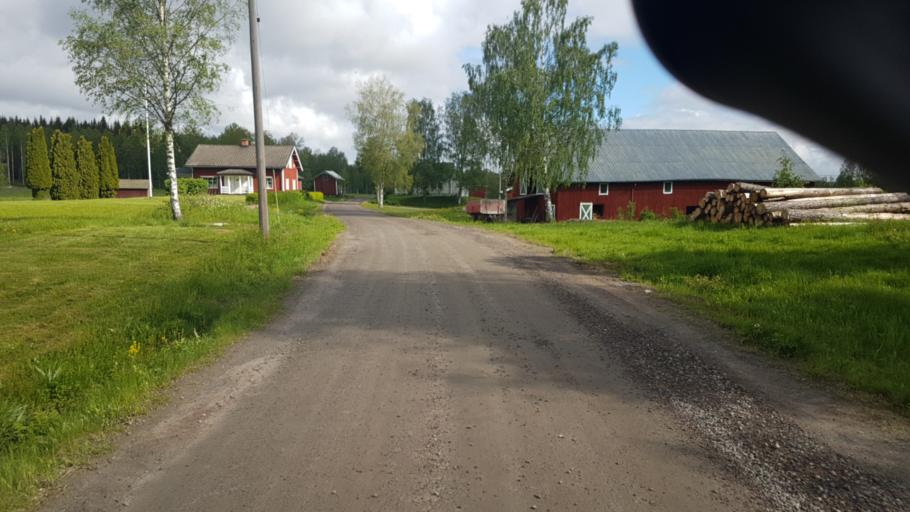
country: NO
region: Ostfold
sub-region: Romskog
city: Romskog
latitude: 59.8564
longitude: 11.9662
